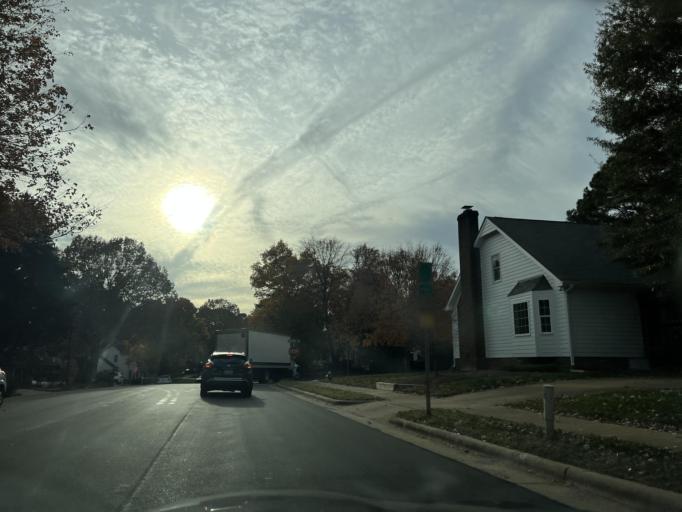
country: US
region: North Carolina
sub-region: Wake County
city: Wake Forest
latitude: 35.8971
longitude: -78.5958
